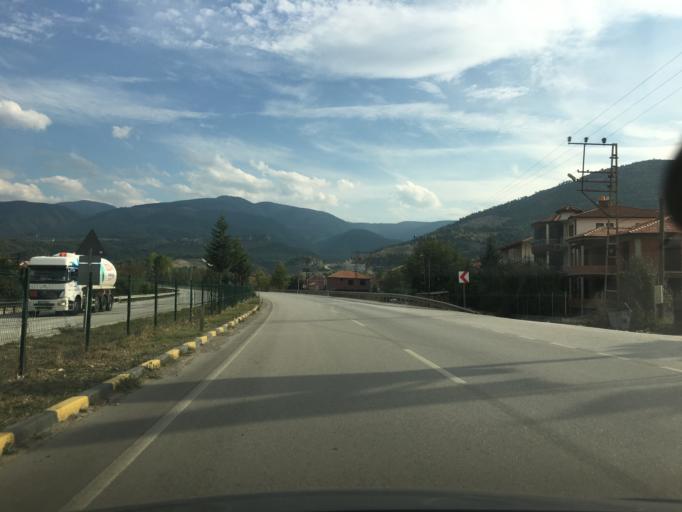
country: TR
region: Karabuk
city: Karabuk
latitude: 41.1034
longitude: 32.6691
